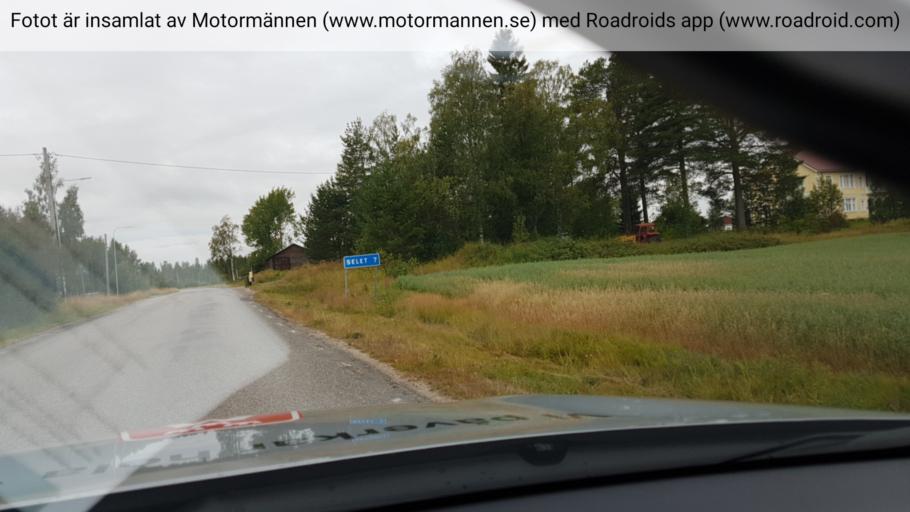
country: SE
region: Norrbotten
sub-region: Bodens Kommun
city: Saevast
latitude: 65.6753
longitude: 21.7971
